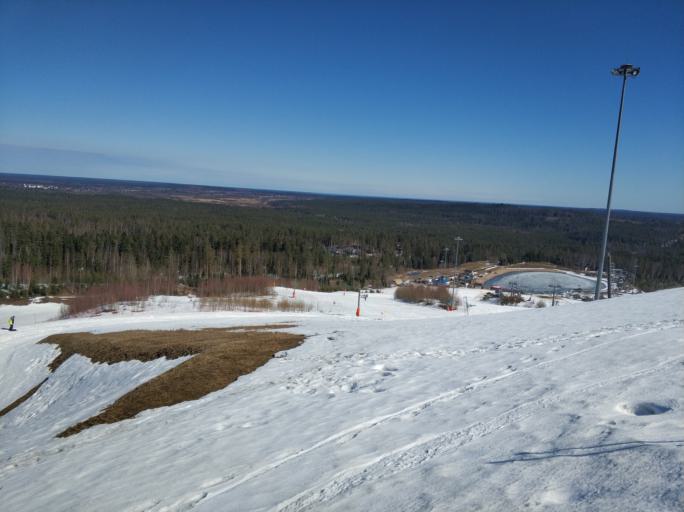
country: RU
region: Leningrad
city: Sosnovo
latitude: 60.5149
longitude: 30.2126
